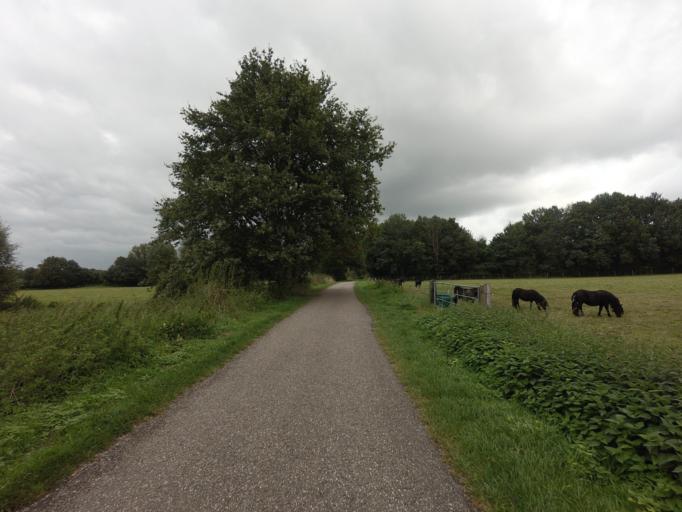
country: NL
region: Overijssel
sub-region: Gemeente Losser
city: Losser
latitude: 52.2585
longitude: 7.0183
